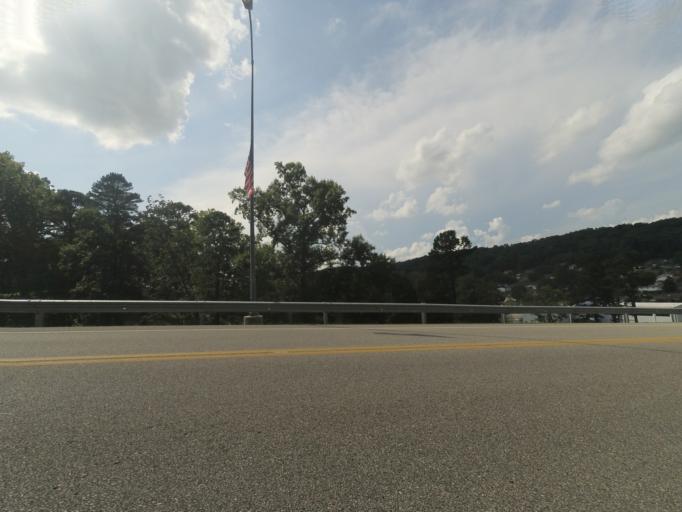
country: US
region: Ohio
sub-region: Lawrence County
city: Burlington
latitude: 38.3819
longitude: -82.5176
